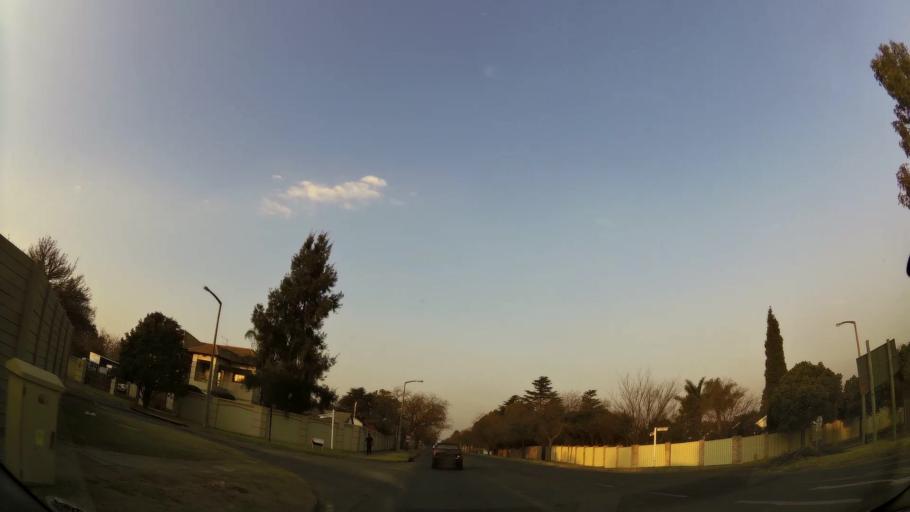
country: ZA
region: Gauteng
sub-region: Ekurhuleni Metropolitan Municipality
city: Benoni
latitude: -26.1739
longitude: 28.3330
